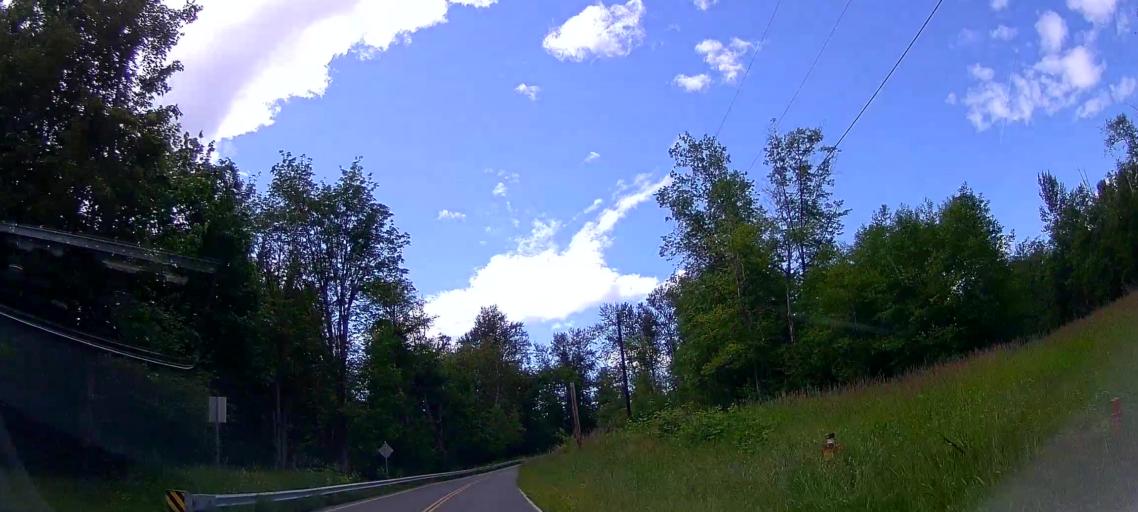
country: US
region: Washington
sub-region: Skagit County
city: Sedro-Woolley
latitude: 48.5287
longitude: -122.2143
